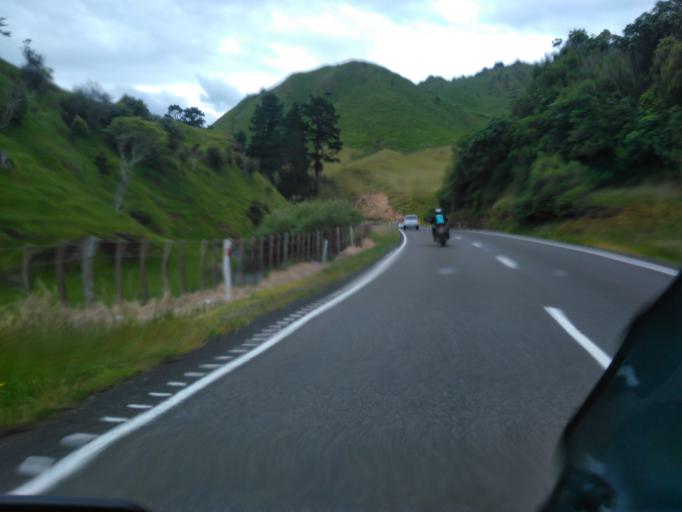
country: NZ
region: Bay of Plenty
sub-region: Opotiki District
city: Opotiki
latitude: -38.3722
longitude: 177.4650
